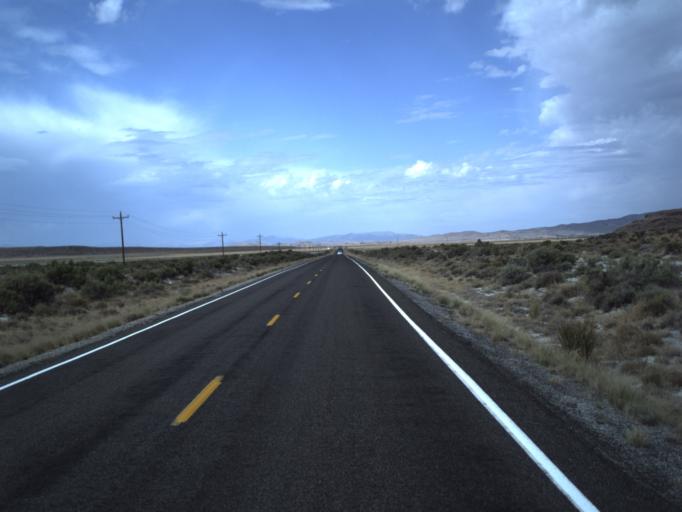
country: US
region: Utah
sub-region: Tooele County
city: Wendover
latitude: 41.4232
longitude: -113.8733
